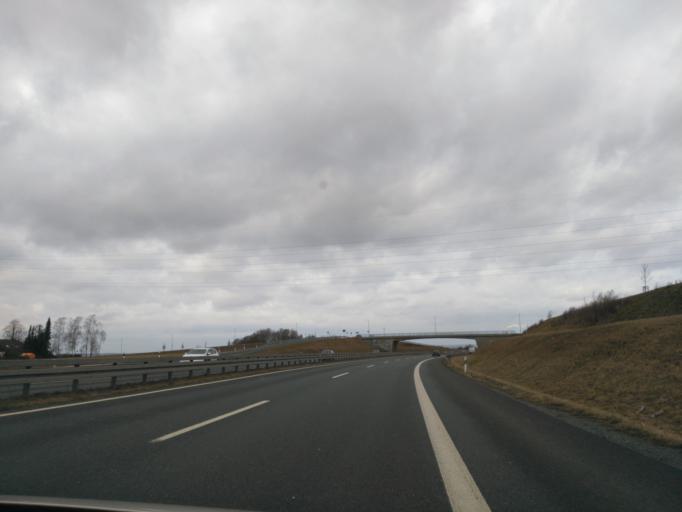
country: DE
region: Saxony
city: Hilbersdorf
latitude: 50.7988
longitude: 12.9757
